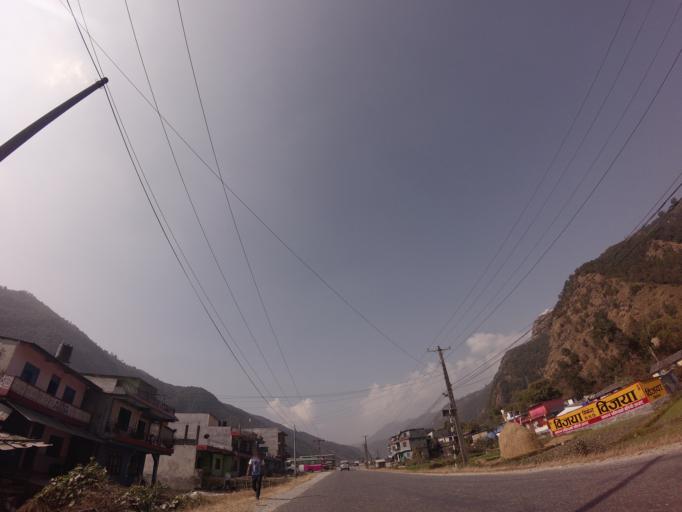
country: NP
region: Western Region
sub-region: Gandaki Zone
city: Pokhara
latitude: 28.2855
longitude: 83.9036
